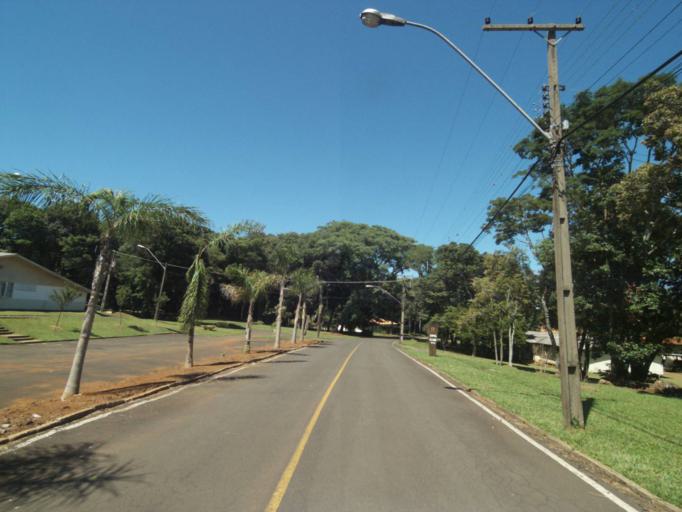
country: BR
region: Parana
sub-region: Chopinzinho
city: Chopinzinho
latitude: -25.7987
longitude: -52.0987
